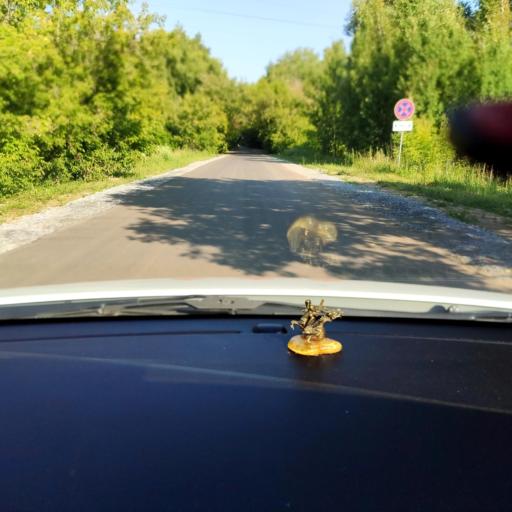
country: RU
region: Tatarstan
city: Stolbishchi
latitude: 55.6995
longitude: 49.2223
